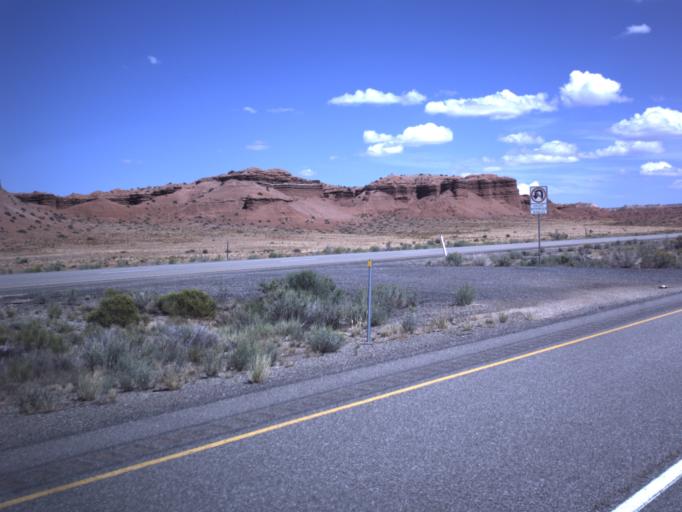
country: US
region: Utah
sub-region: Emery County
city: Ferron
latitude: 38.8452
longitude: -111.0511
